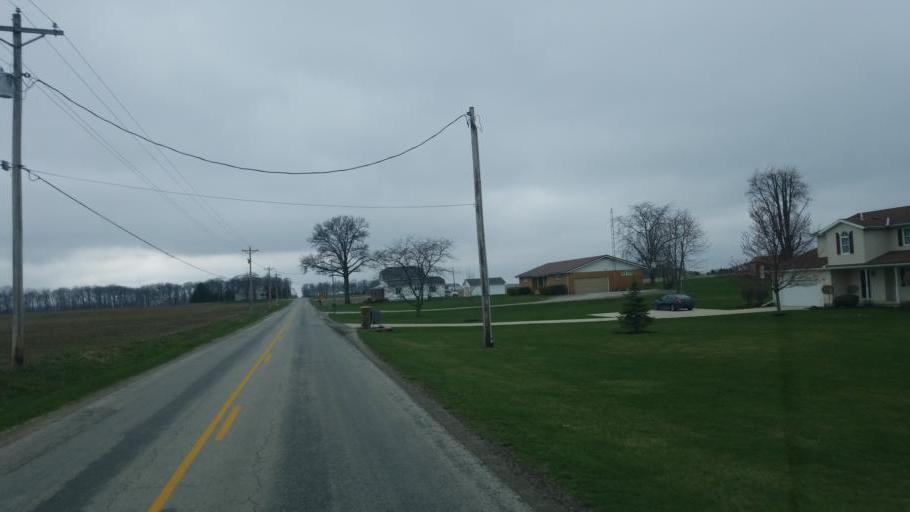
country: US
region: Ohio
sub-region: Marion County
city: Marion
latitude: 40.6878
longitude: -83.2342
